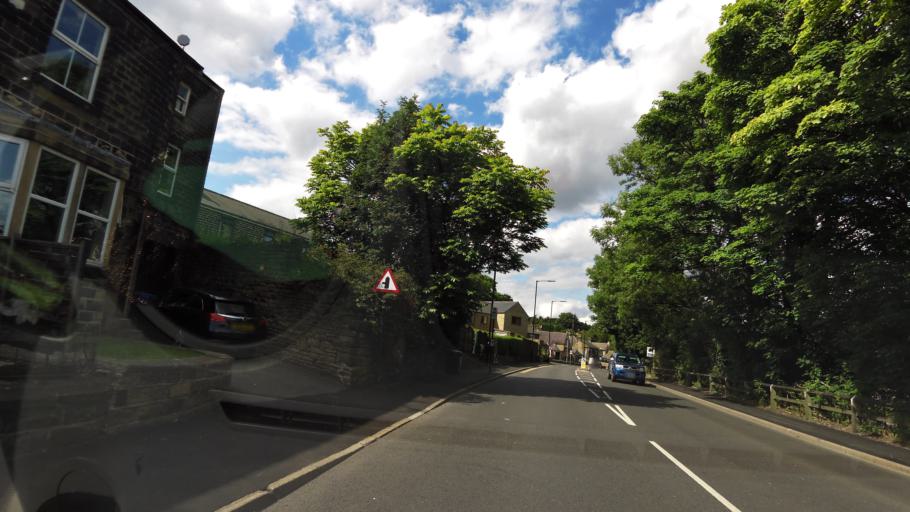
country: GB
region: England
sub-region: Sheffield
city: Chapletown
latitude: 53.4399
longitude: -1.4961
